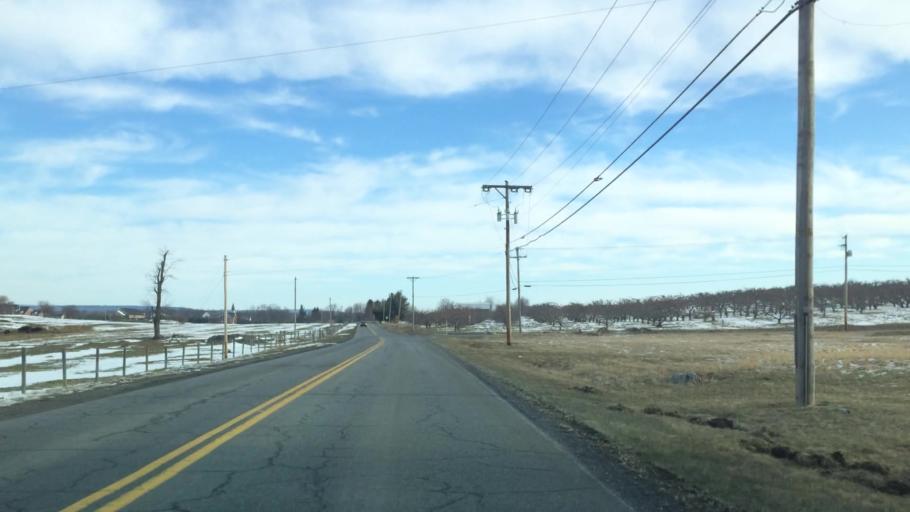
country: US
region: Virginia
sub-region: City of Winchester
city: Winchester
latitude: 39.2587
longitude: -78.1335
